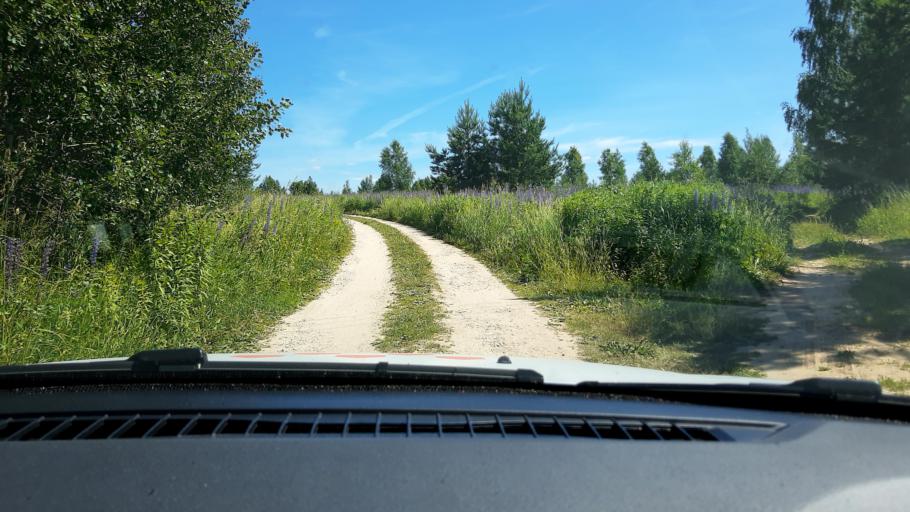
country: RU
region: Nizjnij Novgorod
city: Surovatikha
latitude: 55.8698
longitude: 43.9662
